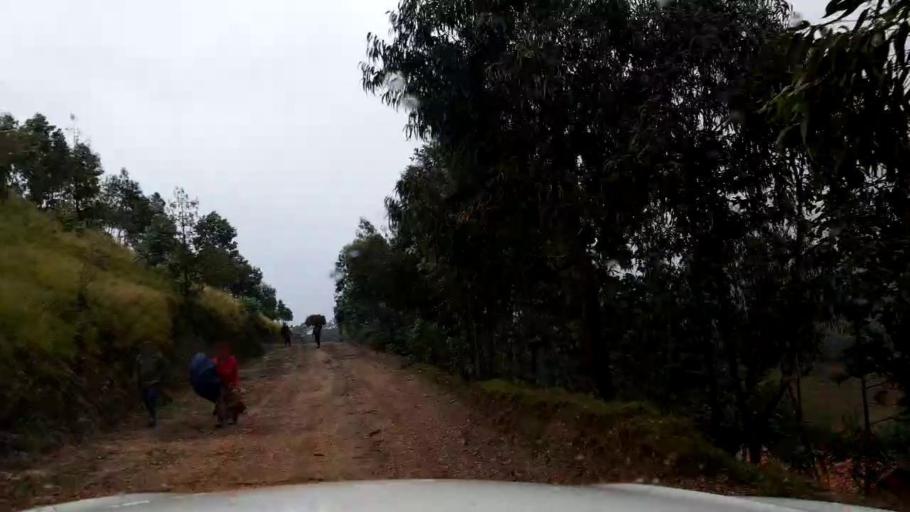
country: RW
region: Western Province
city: Kibuye
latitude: -2.0148
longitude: 29.4695
